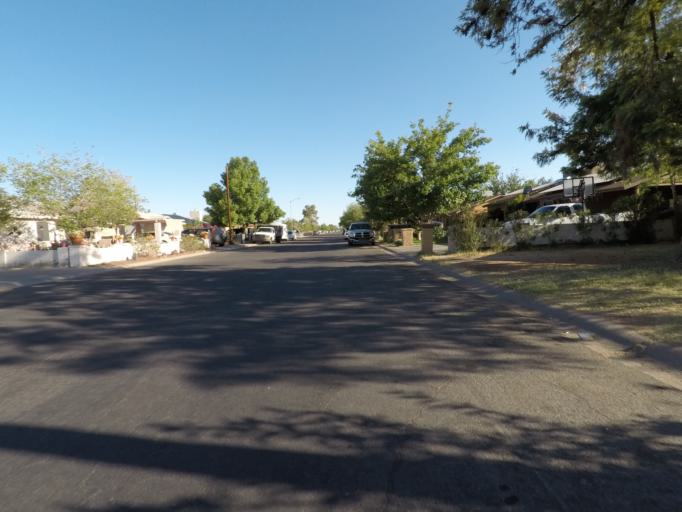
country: US
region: Arizona
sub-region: Maricopa County
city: Glendale
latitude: 33.5805
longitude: -112.0956
